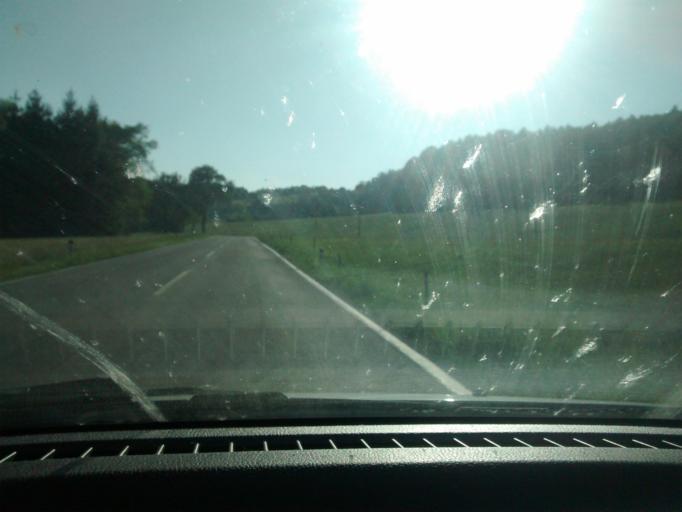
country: AT
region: Lower Austria
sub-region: Politischer Bezirk Lilienfeld
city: Hainfeld
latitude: 48.0558
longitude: 15.8079
